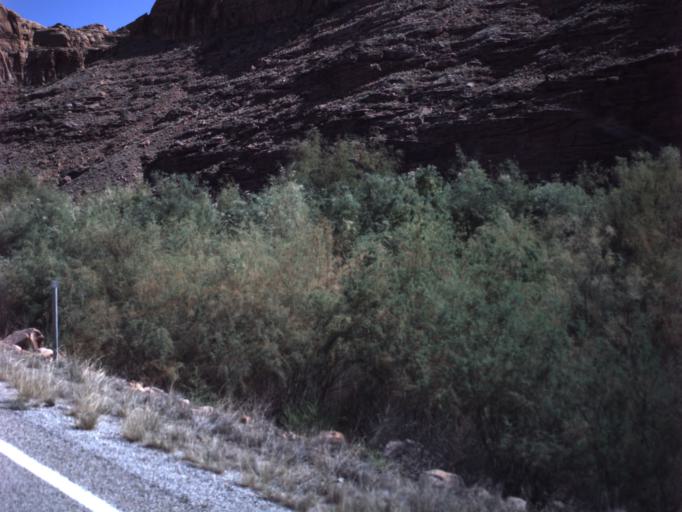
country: US
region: Utah
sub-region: Grand County
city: Moab
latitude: 38.5301
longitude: -109.6144
